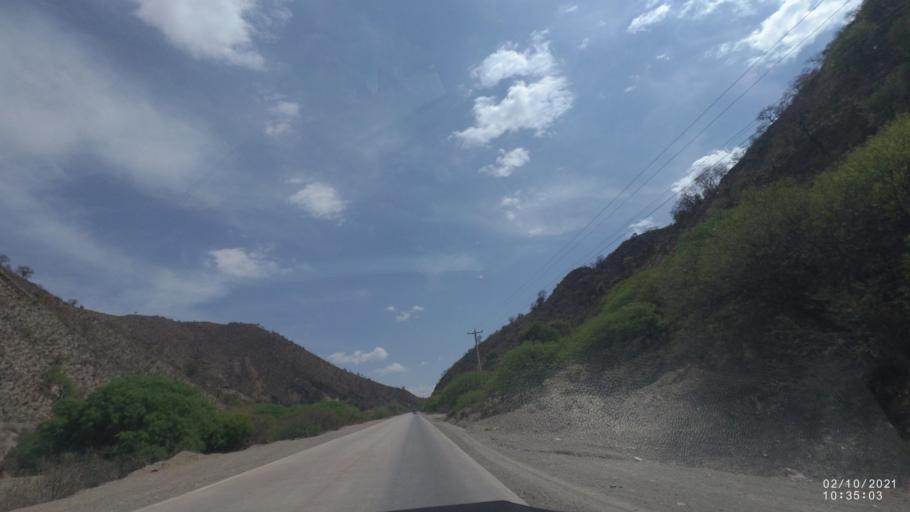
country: BO
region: Cochabamba
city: Capinota
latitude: -17.6663
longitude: -66.2575
